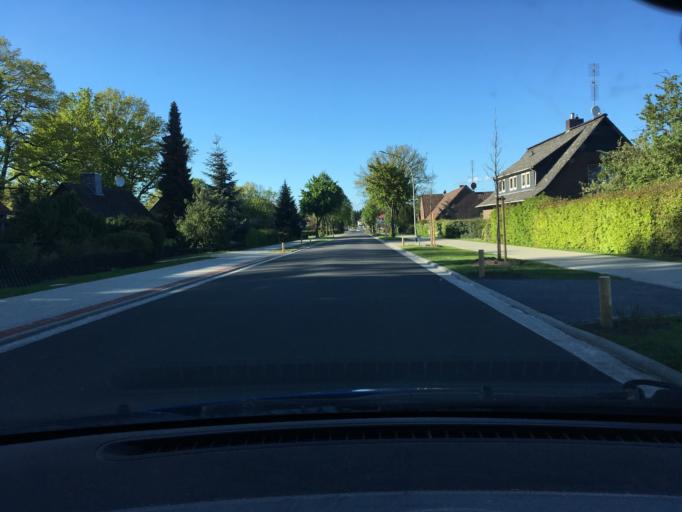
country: DE
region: Lower Saxony
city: Schneverdingen
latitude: 53.0761
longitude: 9.8633
